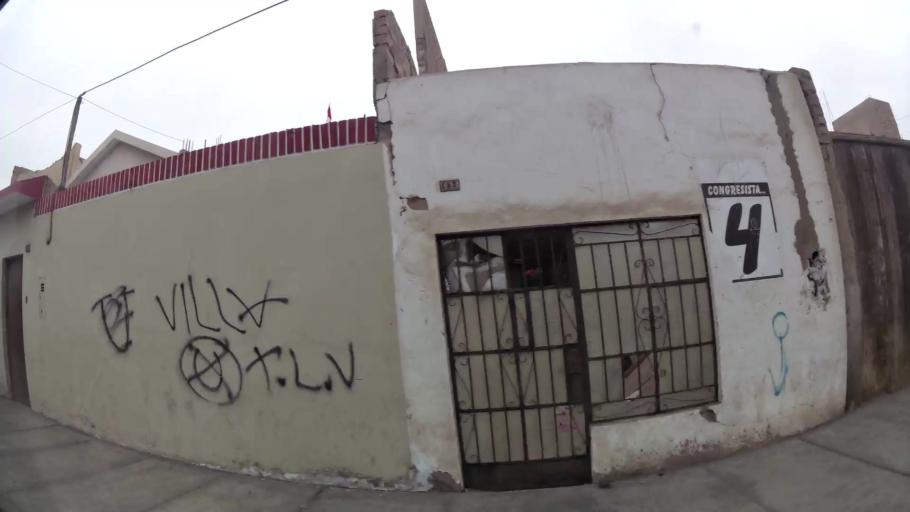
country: PE
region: Ica
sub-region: Provincia de Pisco
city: Pisco
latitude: -13.7084
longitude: -76.2031
